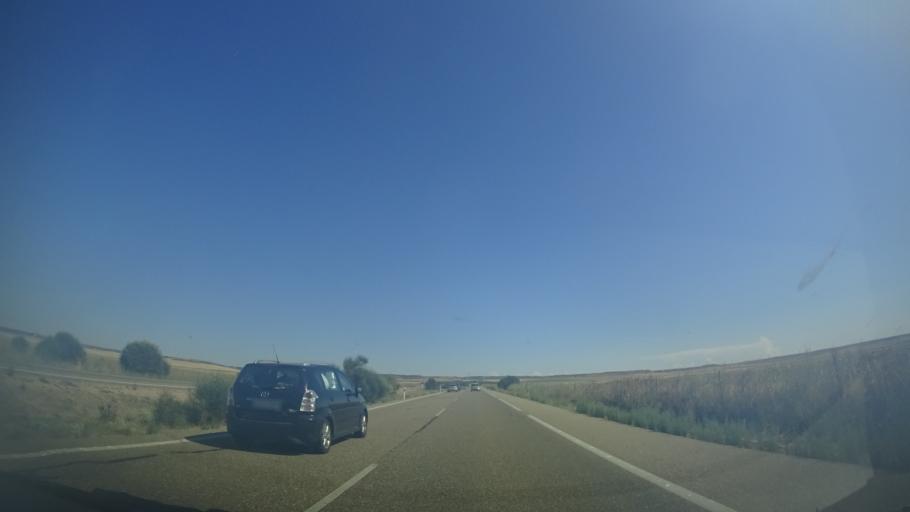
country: ES
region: Castille and Leon
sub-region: Provincia de Valladolid
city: Villardefrades
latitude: 41.7459
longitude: -5.2764
